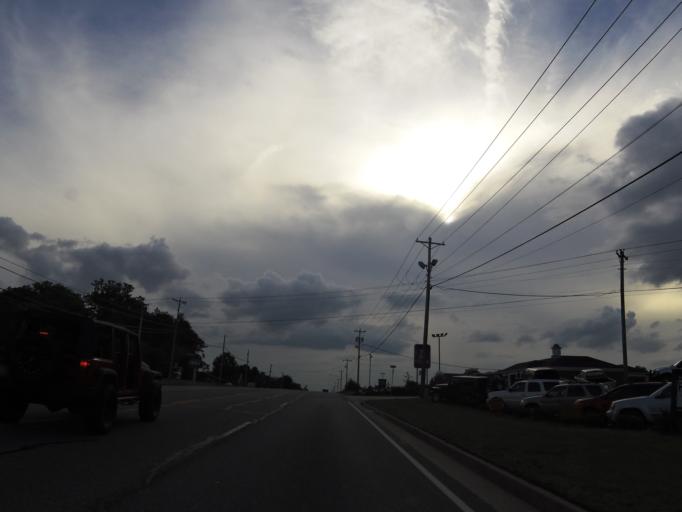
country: US
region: Tennessee
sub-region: Blount County
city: Maryville
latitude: 35.7558
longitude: -83.9366
